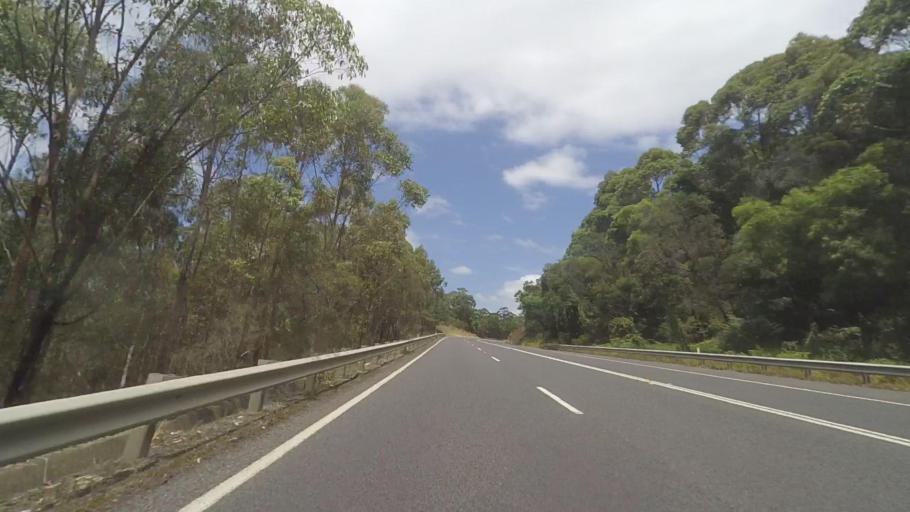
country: AU
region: New South Wales
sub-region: Shoalhaven Shire
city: Milton
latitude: -35.2440
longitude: 150.4258
